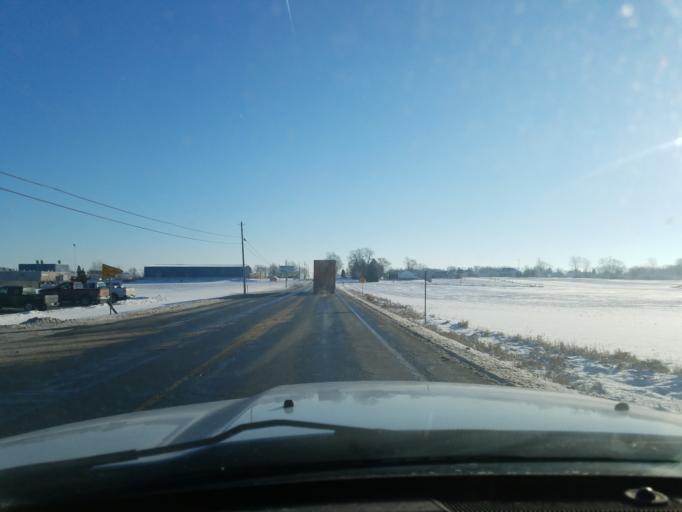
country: US
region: Indiana
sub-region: Noble County
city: Kendallville
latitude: 41.4524
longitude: -85.3131
